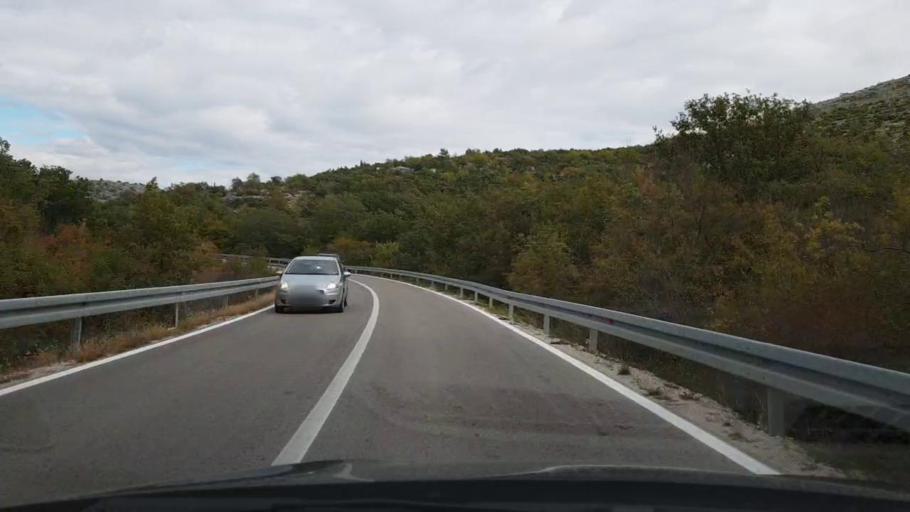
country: BA
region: Republika Srpska
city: Trebinje
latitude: 42.6810
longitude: 18.3001
